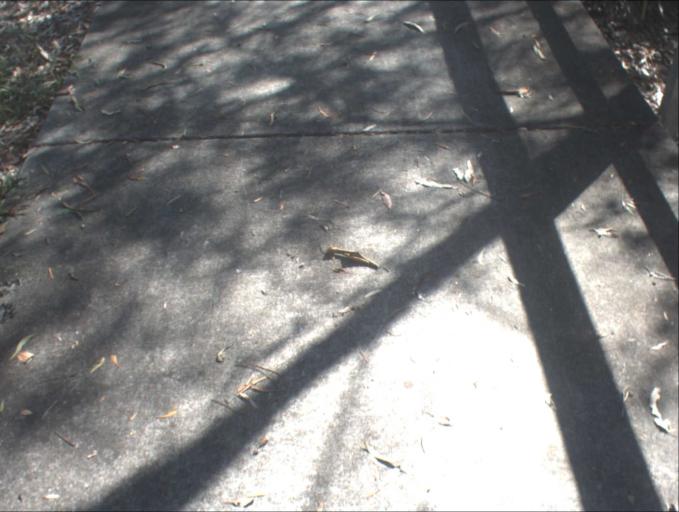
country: AU
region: Queensland
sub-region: Logan
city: Windaroo
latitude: -27.7199
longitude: 153.1727
